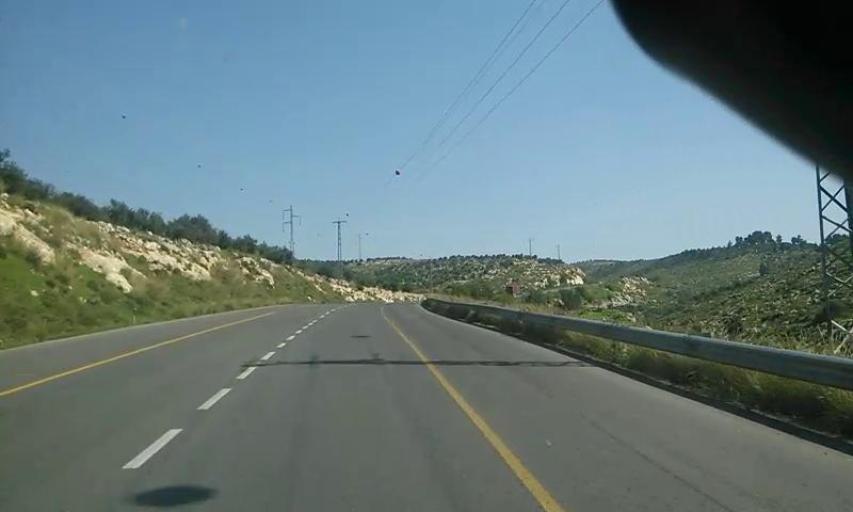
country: PS
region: West Bank
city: Idhna
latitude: 31.5663
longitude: 34.9905
